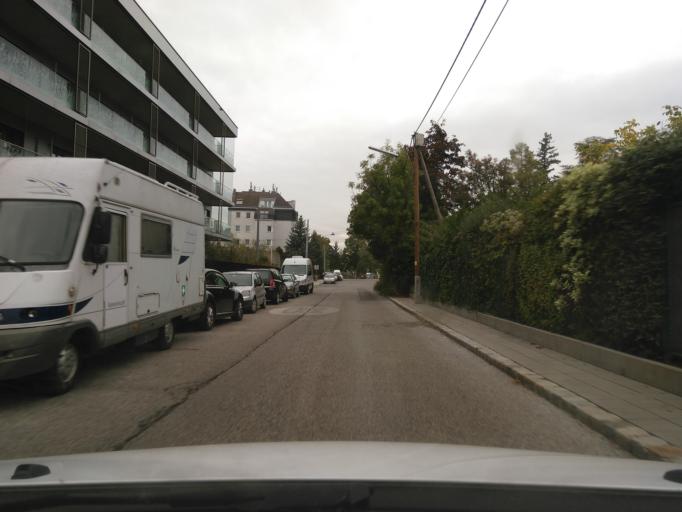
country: AT
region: Lower Austria
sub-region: Politischer Bezirk Modling
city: Perchtoldsdorf
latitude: 48.1988
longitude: 16.2861
